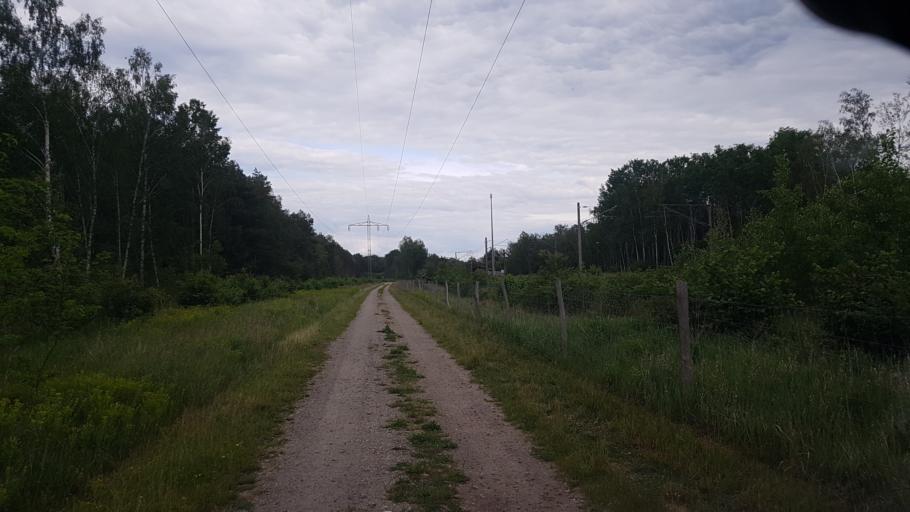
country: DE
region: Brandenburg
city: Trobitz
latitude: 51.6010
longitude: 13.4400
